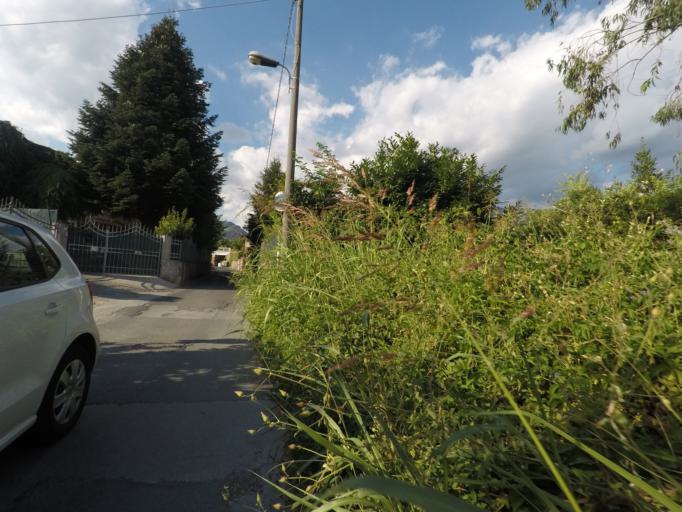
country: IT
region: Tuscany
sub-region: Provincia di Massa-Carrara
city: Capanne-Prato-Cinquale
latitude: 44.0161
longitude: 10.1453
